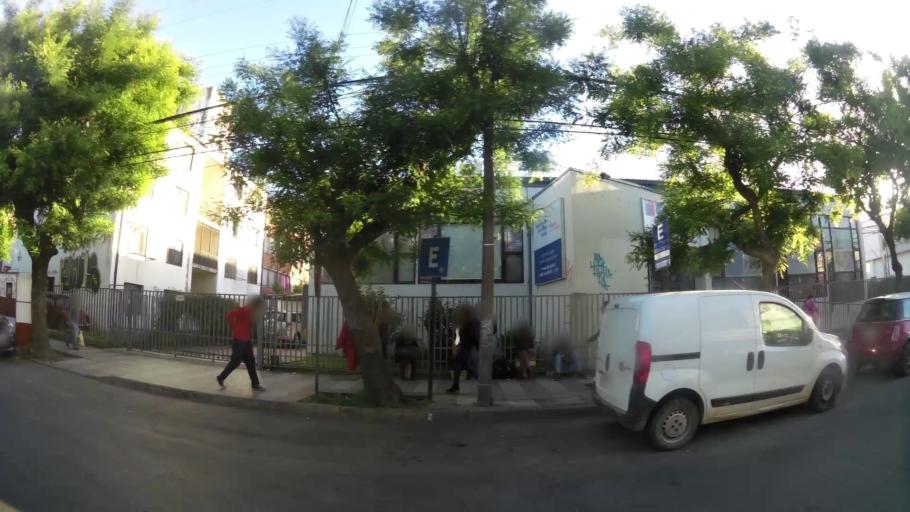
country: CL
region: Valparaiso
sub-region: Provincia de Valparaiso
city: Vina del Mar
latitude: -33.0246
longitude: -71.5479
